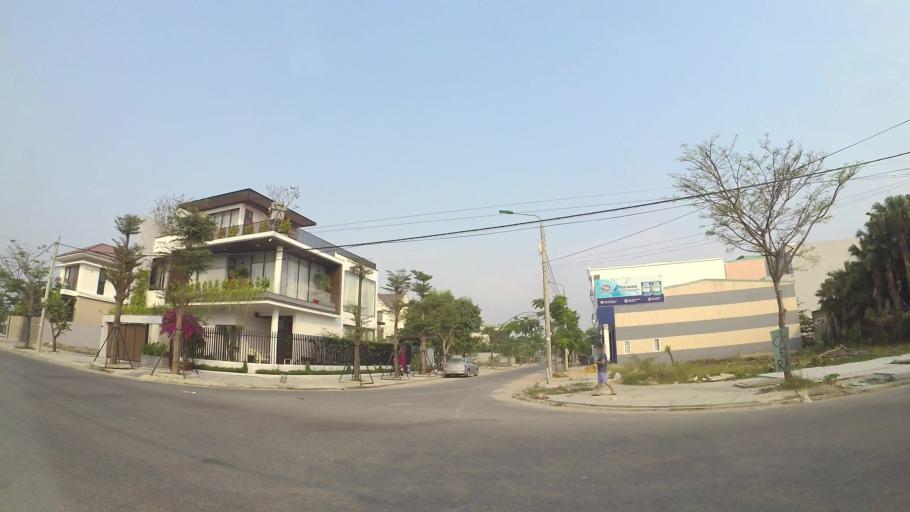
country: VN
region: Da Nang
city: Cam Le
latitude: 16.0116
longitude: 108.2182
